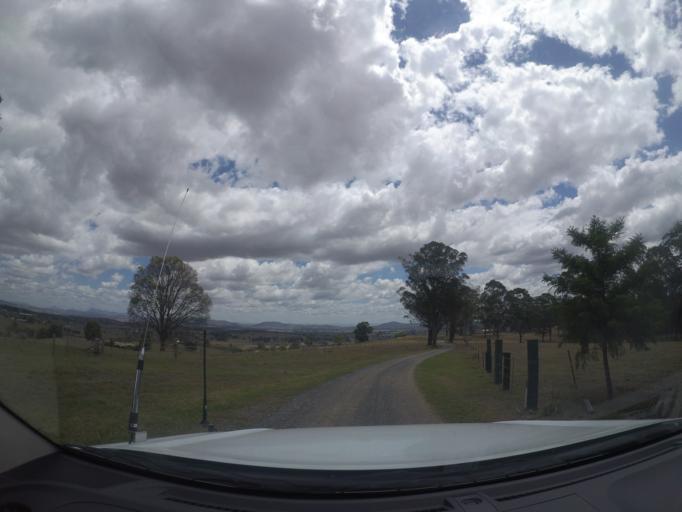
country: AU
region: Queensland
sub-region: Logan
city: Cedar Vale
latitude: -27.9178
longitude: 153.0341
